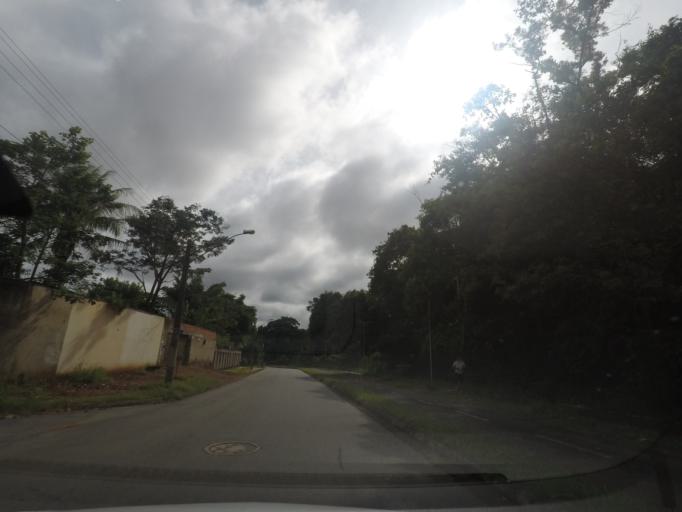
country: BR
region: Goias
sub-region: Goiania
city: Goiania
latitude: -16.7397
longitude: -49.3217
